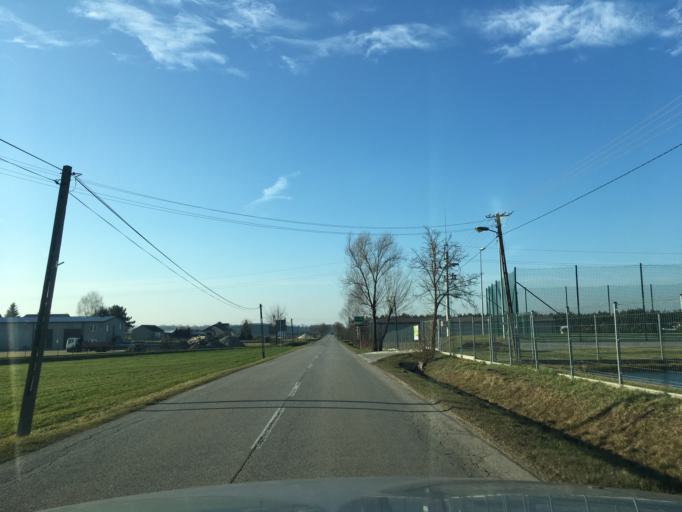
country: PL
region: Masovian Voivodeship
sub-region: Powiat pruszkowski
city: Nadarzyn
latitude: 52.0404
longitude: 20.8141
